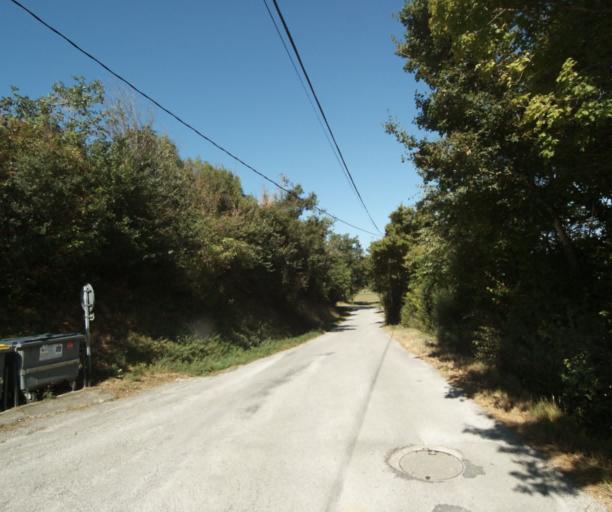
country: FR
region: Midi-Pyrenees
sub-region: Departement du Tarn
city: Soreze
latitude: 43.4475
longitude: 2.0462
